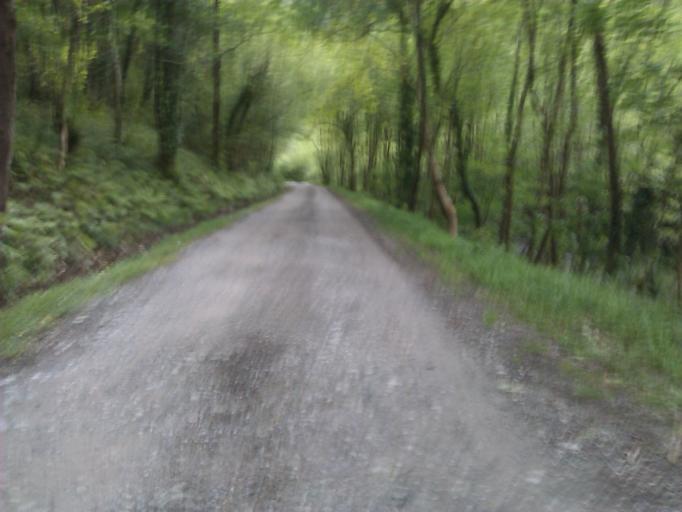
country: ES
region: Navarre
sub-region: Provincia de Navarra
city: Areso
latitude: 43.1195
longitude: -1.9370
